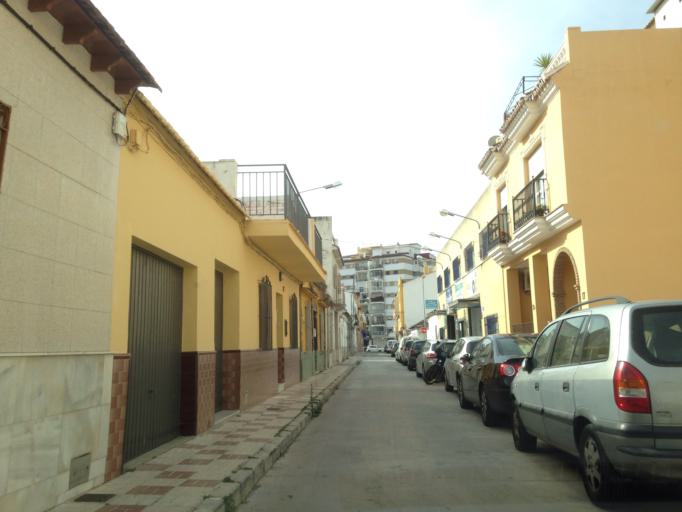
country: ES
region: Andalusia
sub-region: Provincia de Malaga
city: Malaga
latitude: 36.7511
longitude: -4.4224
